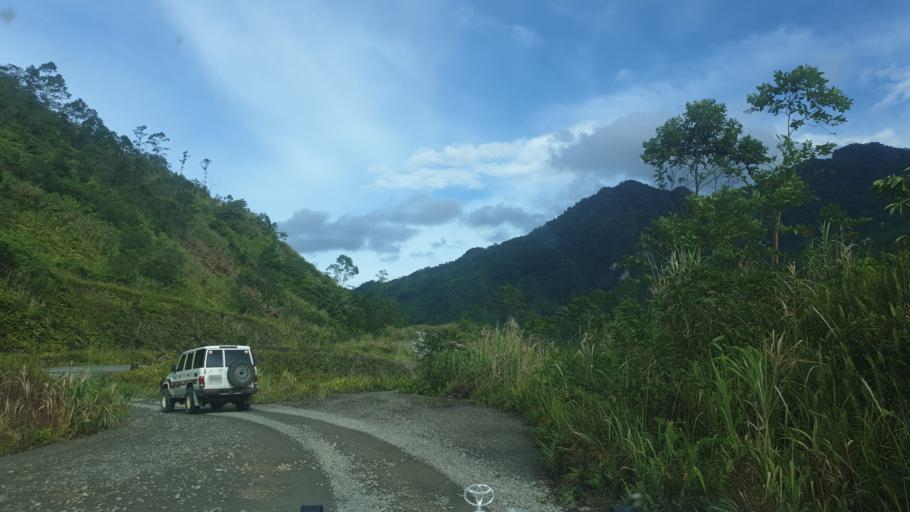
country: PG
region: Bougainville
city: Panguna
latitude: -6.3197
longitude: 155.4812
